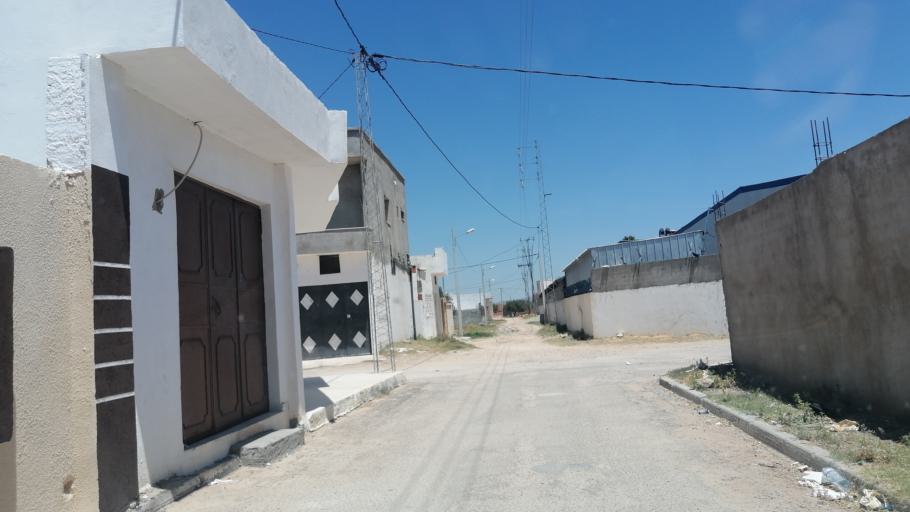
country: TN
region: Al Qayrawan
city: Sbikha
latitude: 36.1221
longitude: 10.0951
